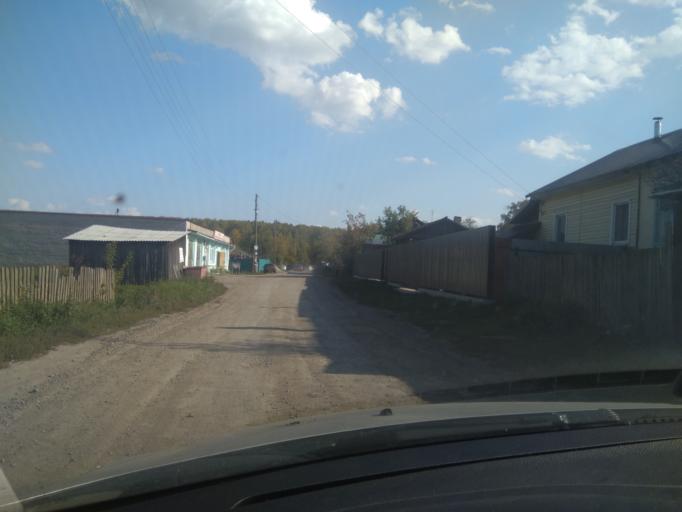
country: RU
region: Sverdlovsk
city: Pokrovskoye
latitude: 56.4336
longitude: 61.5927
